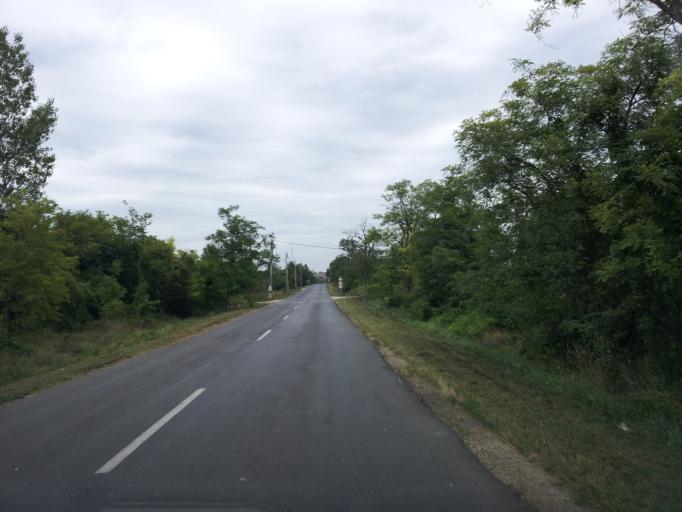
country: HU
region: Pest
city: Tarnok
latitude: 47.3776
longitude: 18.8569
